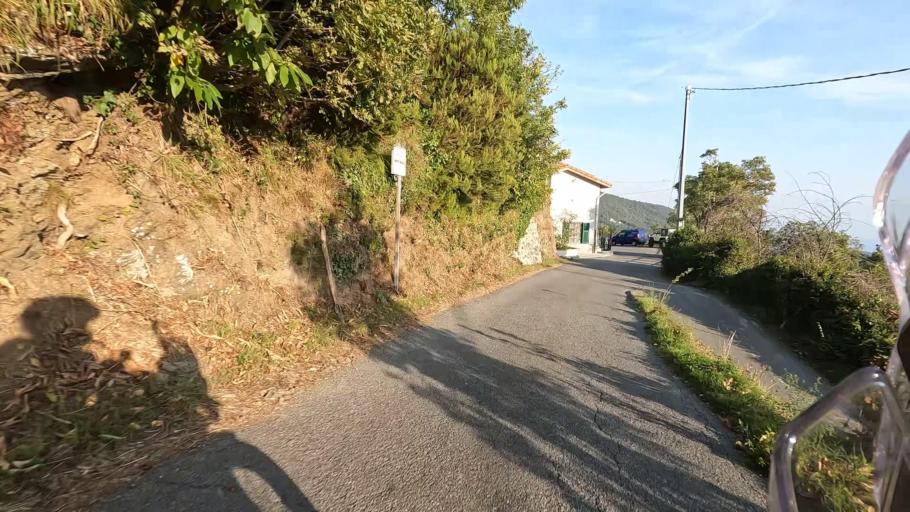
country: IT
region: Liguria
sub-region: Provincia di Savona
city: San Giovanni
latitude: 44.4050
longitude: 8.5289
